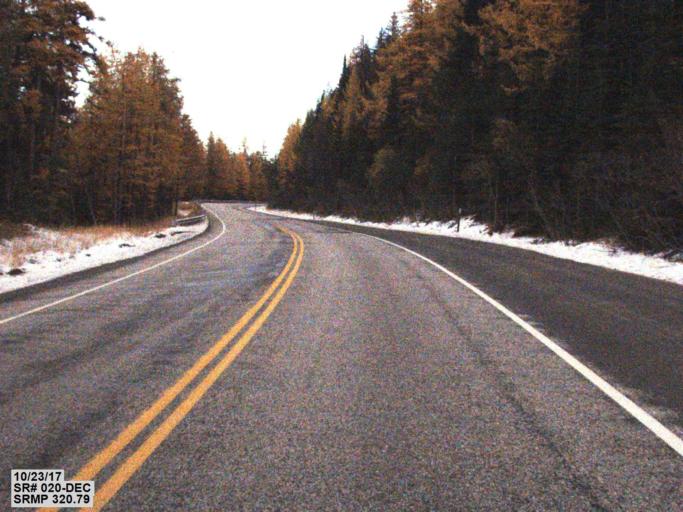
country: US
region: Washington
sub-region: Ferry County
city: Republic
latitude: 48.6067
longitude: -118.4624
